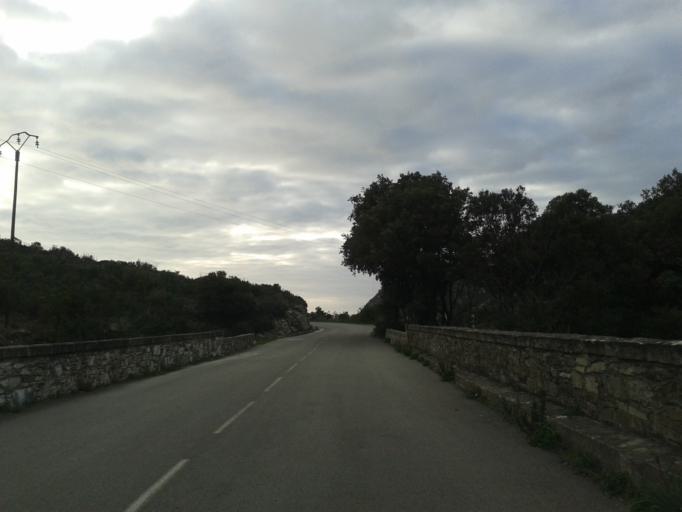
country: FR
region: Corsica
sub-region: Departement de la Haute-Corse
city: Brando
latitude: 42.8648
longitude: 9.3479
